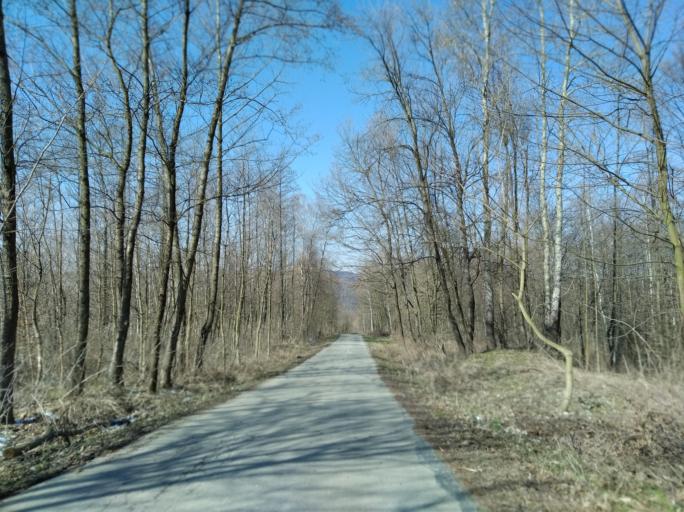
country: PL
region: Subcarpathian Voivodeship
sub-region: Powiat strzyzowski
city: Strzyzow
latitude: 49.8680
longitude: 21.8312
